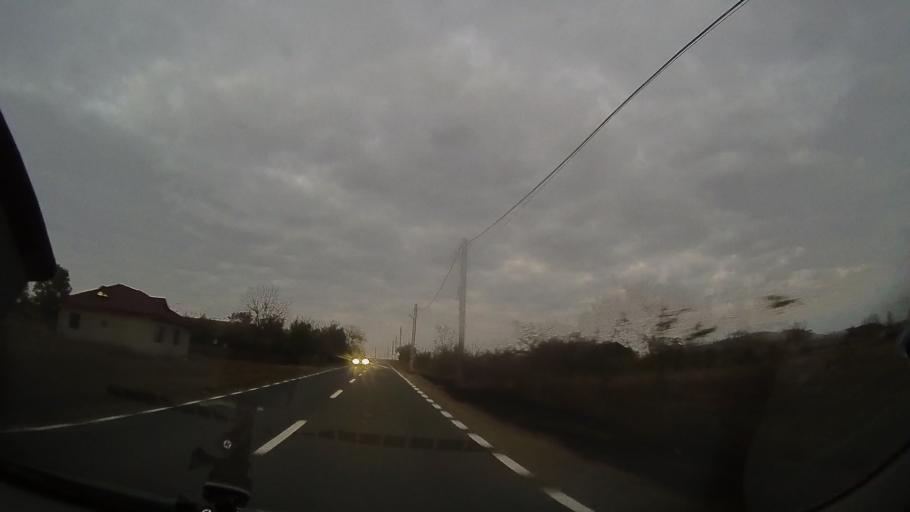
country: RO
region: Tulcea
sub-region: Comuna Nalbant
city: Nicolae Balcescu
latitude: 45.0005
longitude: 28.5934
